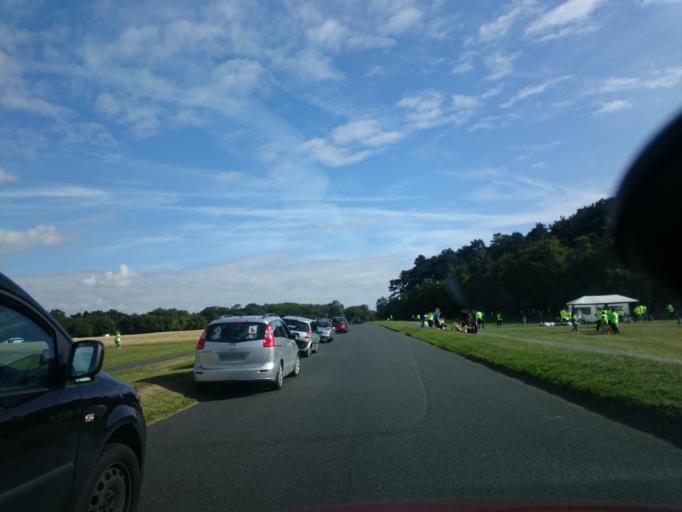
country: IE
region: Leinster
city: Chapelizod
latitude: 53.3540
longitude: -6.3263
